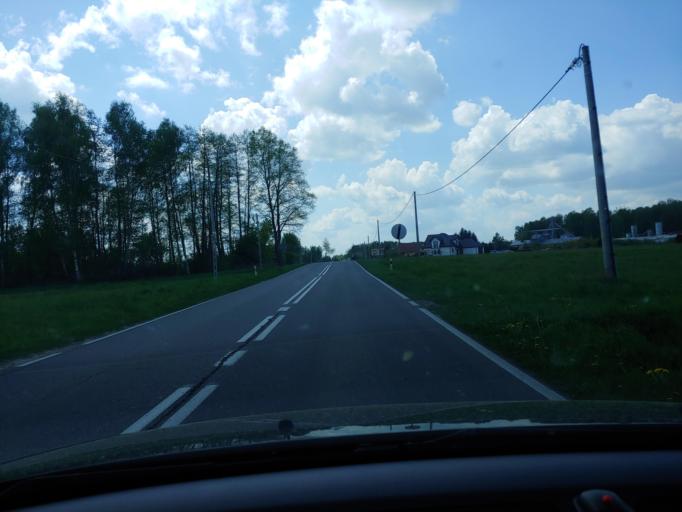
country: PL
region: Subcarpathian Voivodeship
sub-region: Powiat mielecki
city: Wadowice Gorne
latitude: 50.2466
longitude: 21.3096
